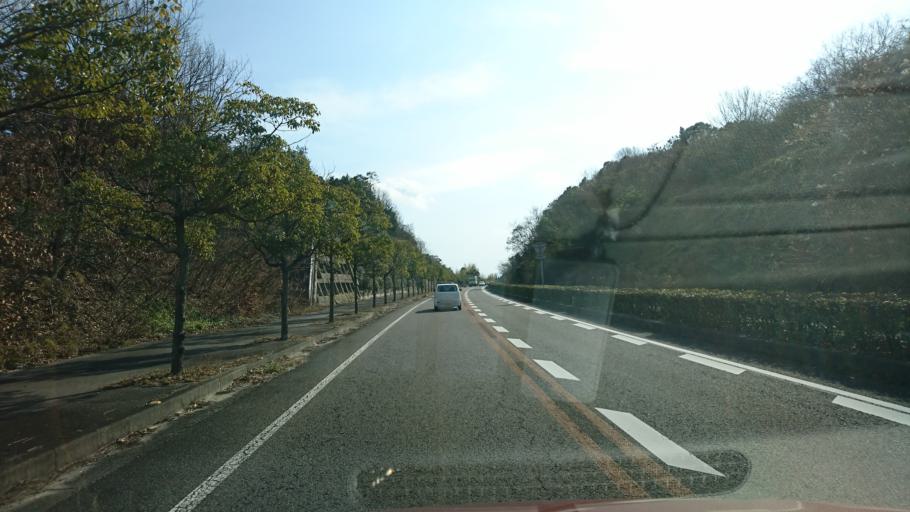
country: JP
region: Ehime
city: Saijo
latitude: 34.0159
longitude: 133.0323
